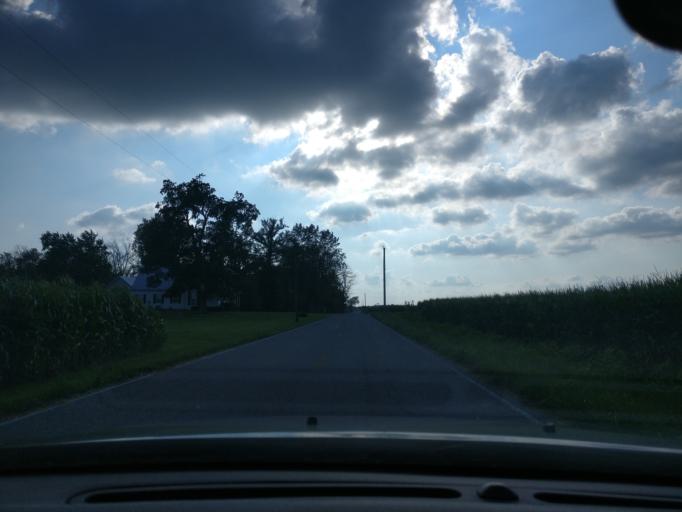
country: US
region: Ohio
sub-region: Clinton County
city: Wilmington
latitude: 39.5363
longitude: -83.8190
